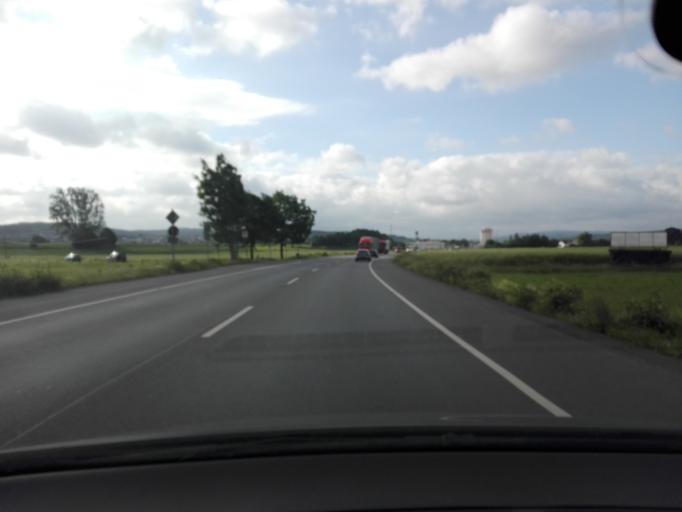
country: DE
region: North Rhine-Westphalia
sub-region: Regierungsbezirk Arnsberg
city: Frondenberg
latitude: 51.4656
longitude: 7.7731
